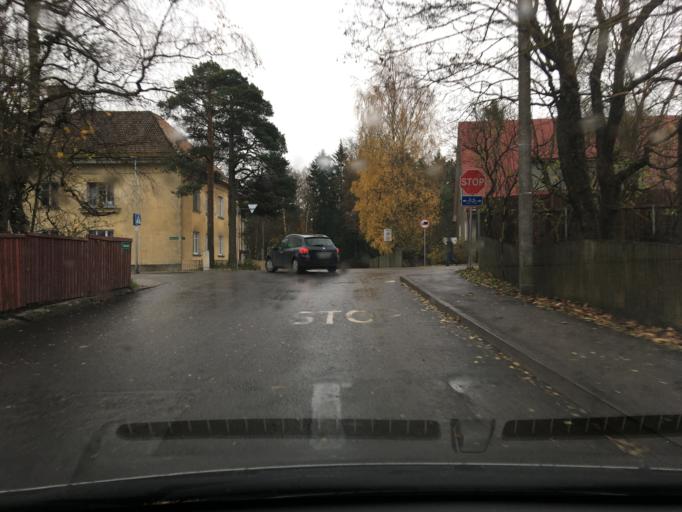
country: EE
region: Harju
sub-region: Tallinna linn
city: Tallinn
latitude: 59.3919
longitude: 24.7179
